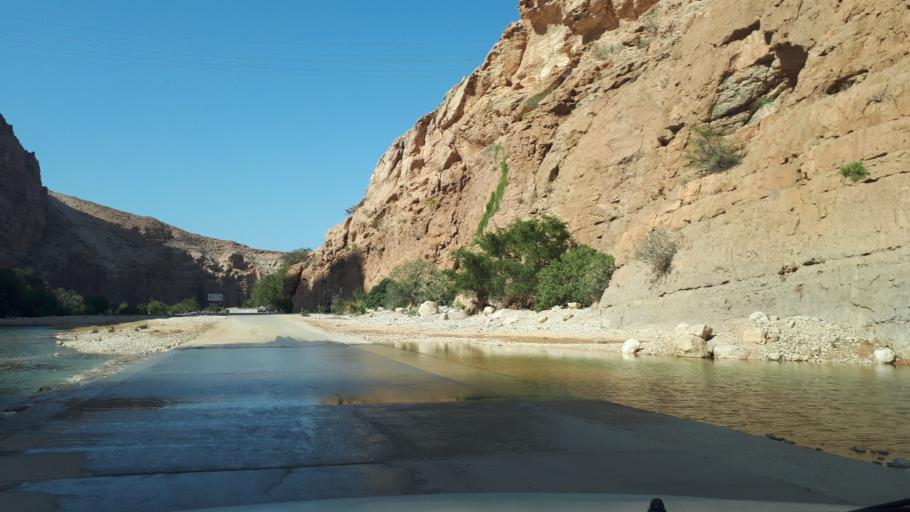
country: OM
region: Ash Sharqiyah
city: Sur
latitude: 22.8197
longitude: 59.2557
